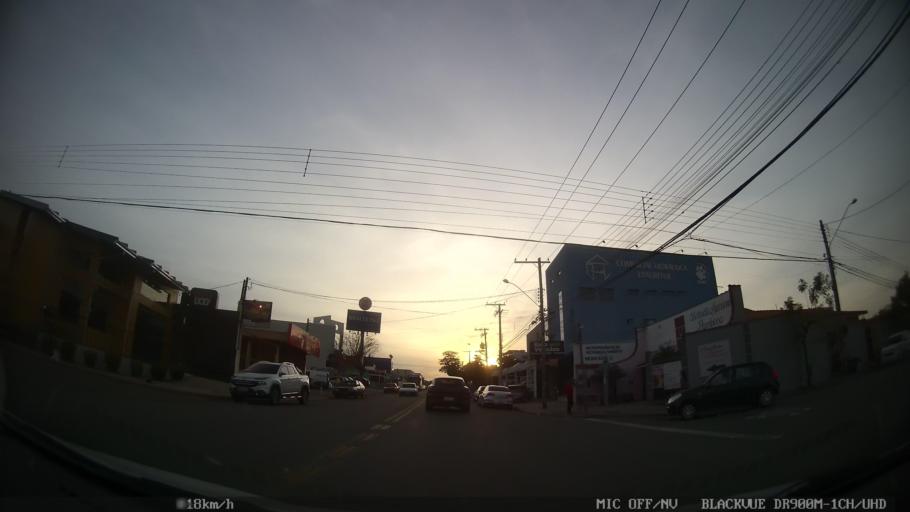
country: BR
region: Sao Paulo
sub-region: Limeira
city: Limeira
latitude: -22.5810
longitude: -47.4169
